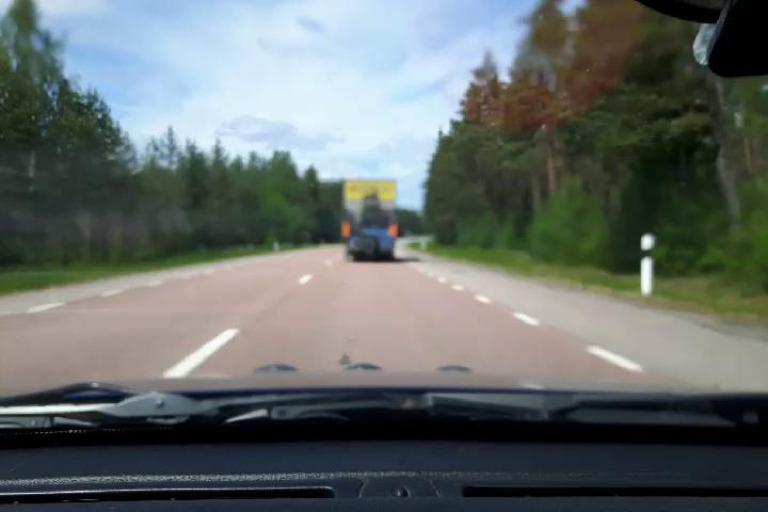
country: SE
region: Uppsala
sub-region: Tierps Kommun
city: Tierp
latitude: 60.1806
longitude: 17.4801
